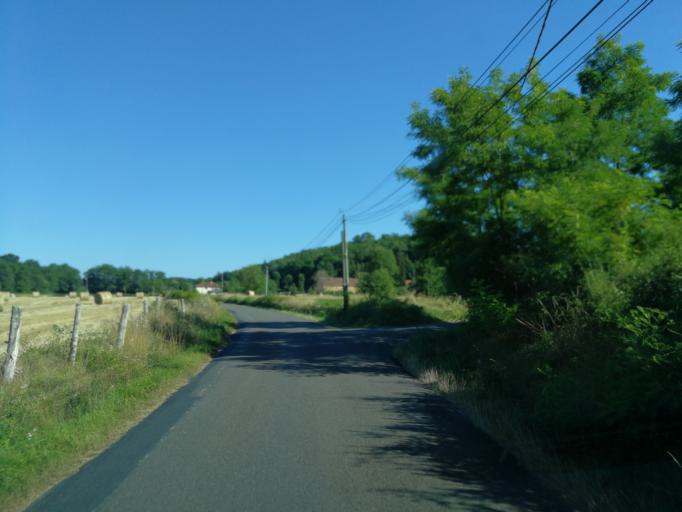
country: FR
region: Midi-Pyrenees
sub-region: Departement du Lot
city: Gourdon
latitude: 44.7638
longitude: 1.3709
